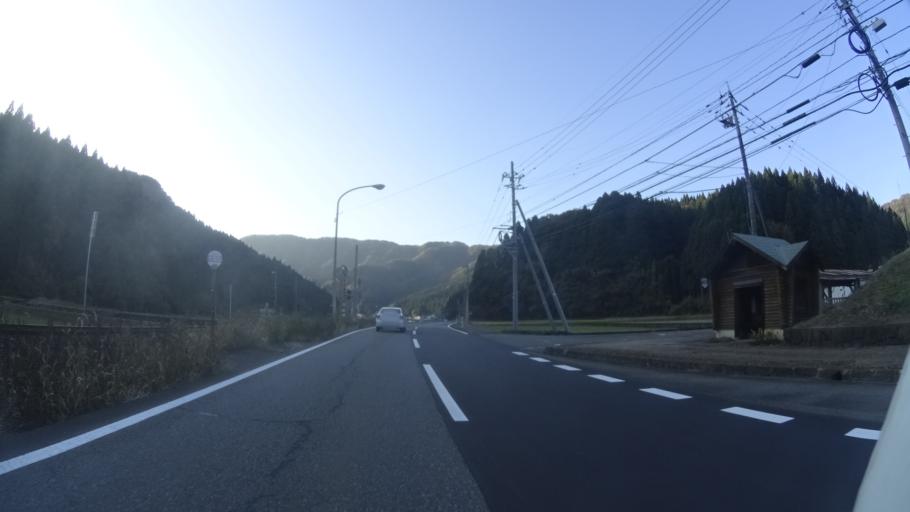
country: JP
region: Fukui
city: Ono
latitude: 36.0056
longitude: 136.3997
